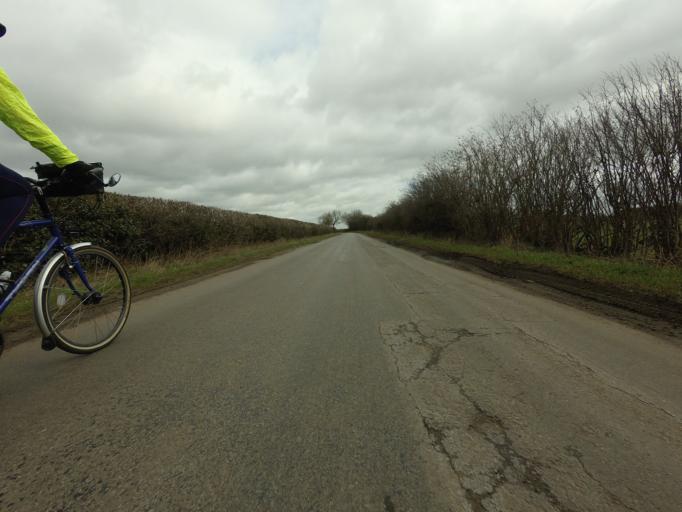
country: GB
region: England
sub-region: Lincolnshire
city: Barrowby
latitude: 52.8741
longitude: -0.6742
